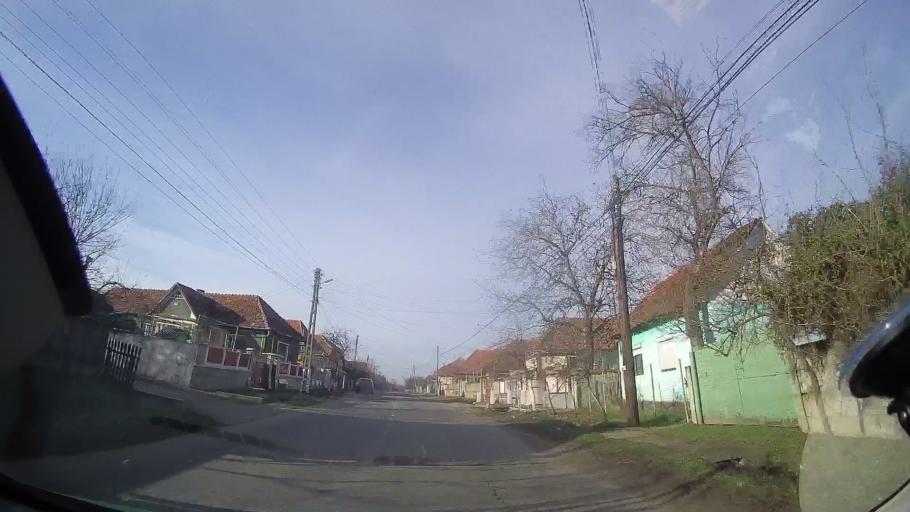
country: RO
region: Bihor
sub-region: Comuna Brusturi
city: Brusturi
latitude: 47.1486
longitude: 22.2539
